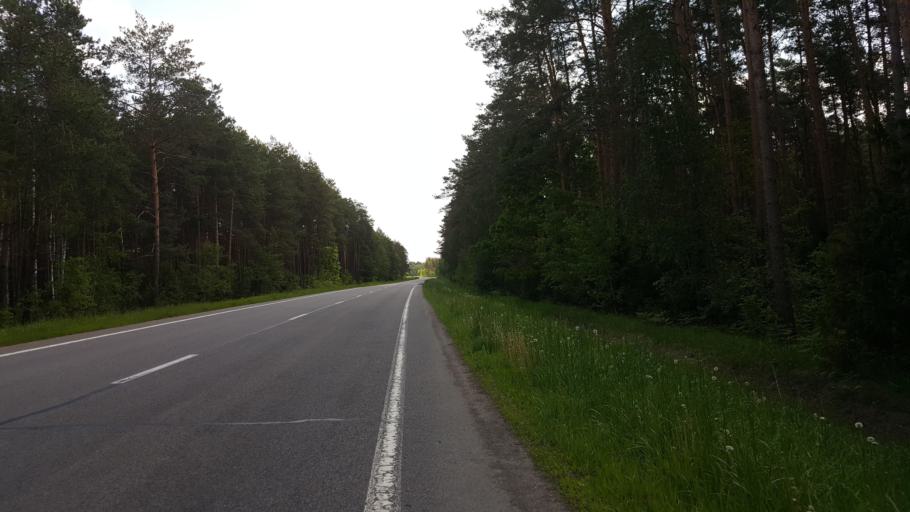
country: BY
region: Brest
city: Zhabinka
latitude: 52.3979
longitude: 24.0504
